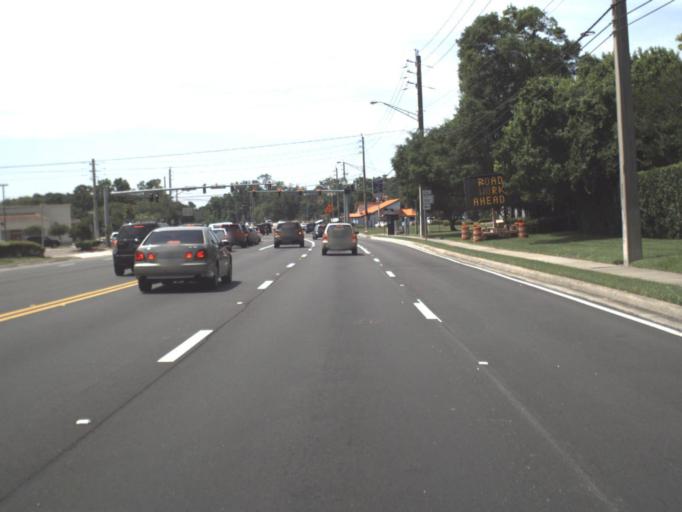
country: US
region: Florida
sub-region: Clay County
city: Orange Park
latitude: 30.2189
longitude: -81.6170
